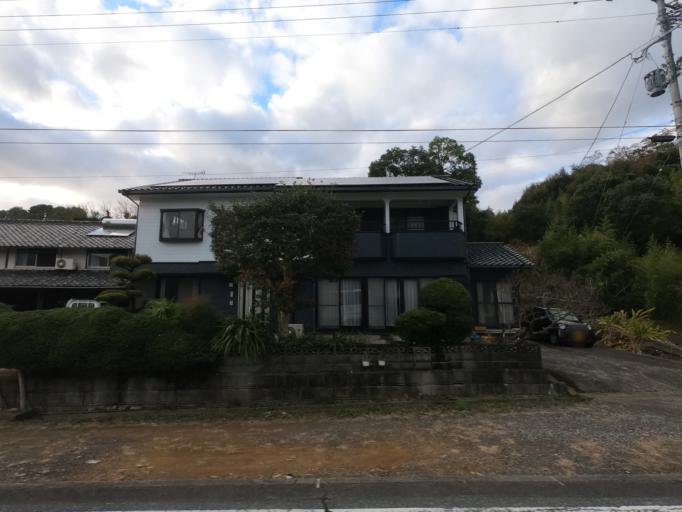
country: JP
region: Kumamoto
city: Minamata
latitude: 32.2447
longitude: 130.4699
